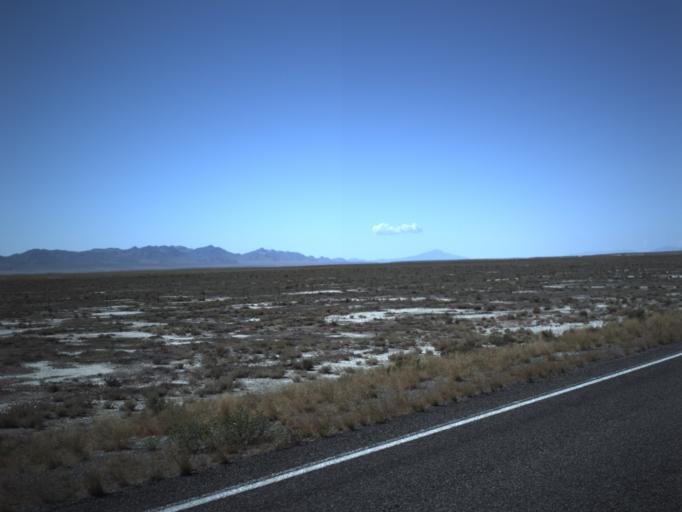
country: US
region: Utah
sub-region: Millard County
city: Delta
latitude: 39.2330
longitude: -112.9274
